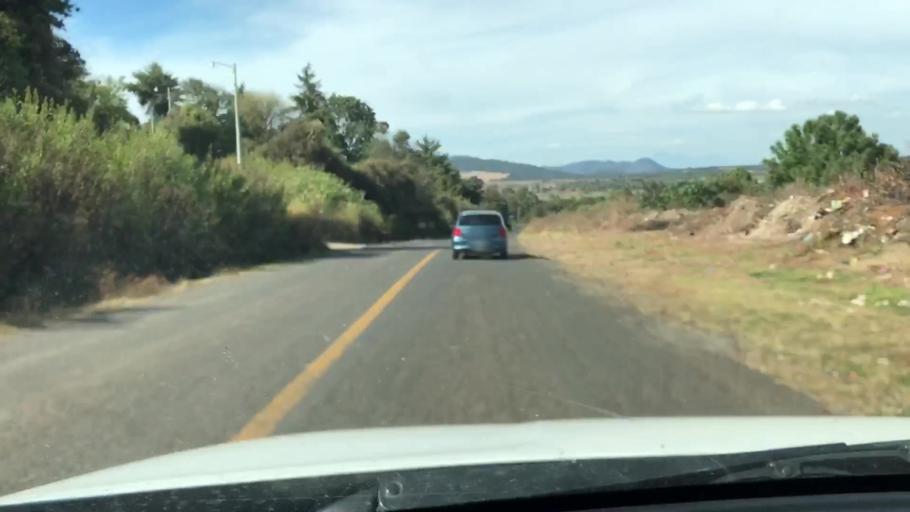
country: MX
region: Jalisco
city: Chiquilistlan
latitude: 20.1446
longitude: -103.7231
